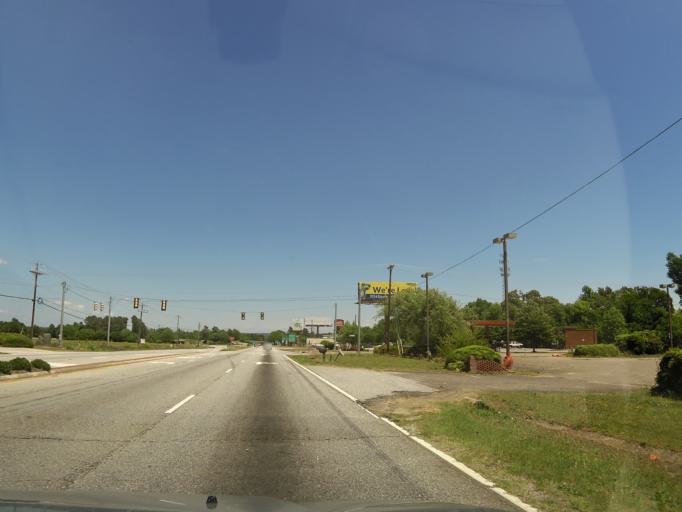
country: US
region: South Carolina
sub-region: Aiken County
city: Clearwater
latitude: 33.4873
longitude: -81.9266
